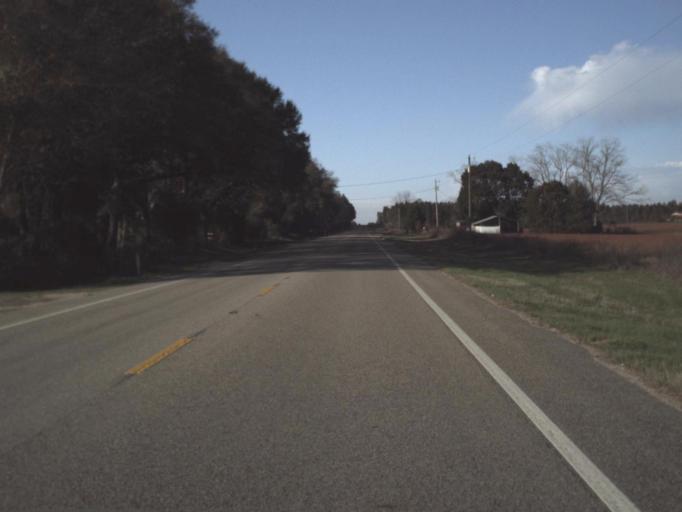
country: US
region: Florida
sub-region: Jackson County
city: Marianna
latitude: 30.5952
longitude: -85.1815
